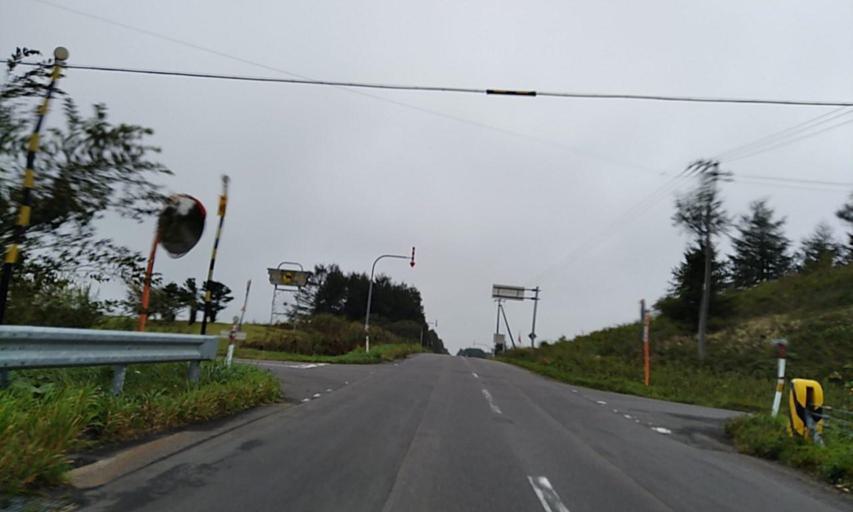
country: JP
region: Hokkaido
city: Shibetsu
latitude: 43.5064
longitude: 144.6640
